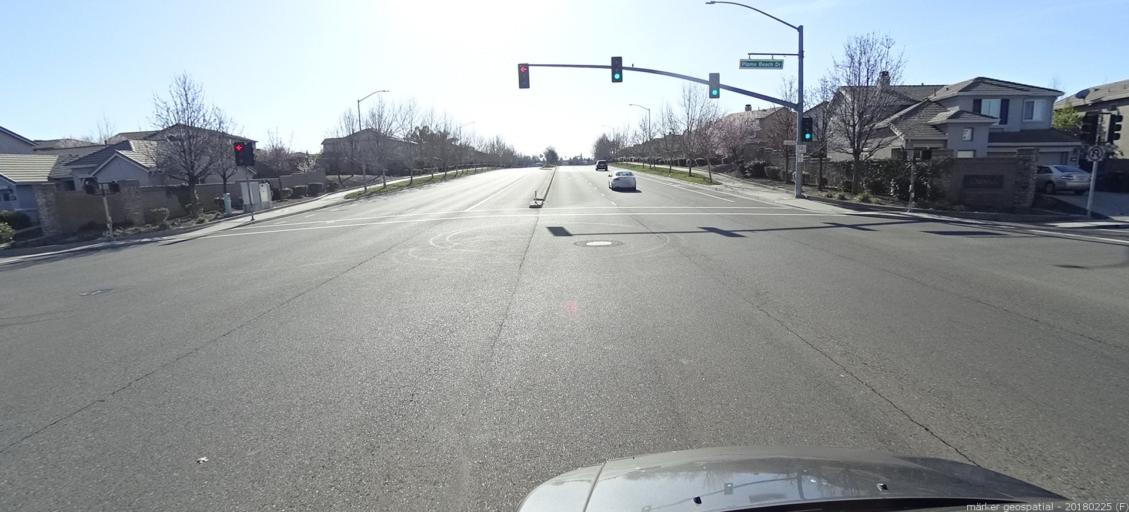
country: US
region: California
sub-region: Sacramento County
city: Antelope
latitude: 38.7079
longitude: -121.3542
